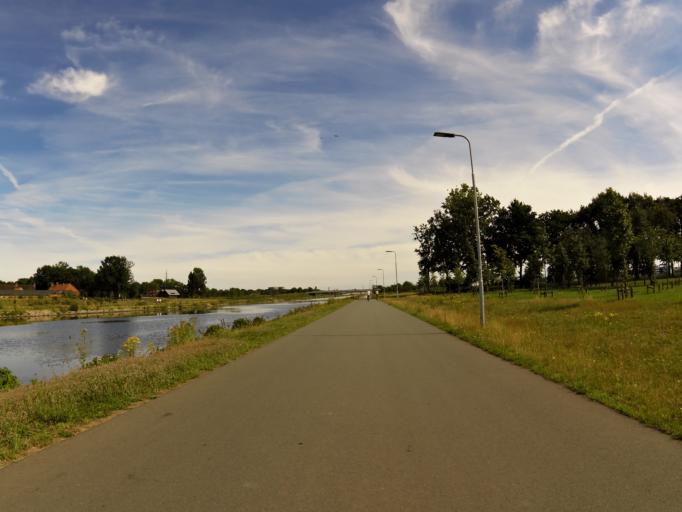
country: NL
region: North Brabant
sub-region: Gemeente 's-Hertogenbosch
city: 's-Hertogenbosch
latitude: 51.7155
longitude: 5.3451
